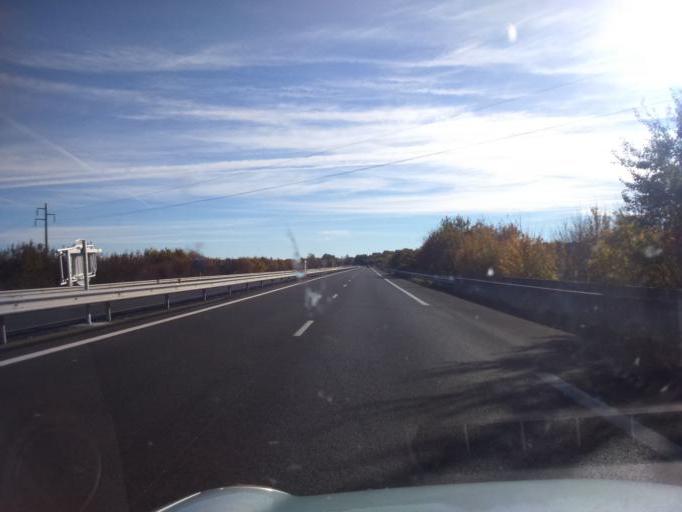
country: FR
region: Poitou-Charentes
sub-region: Departement de la Charente-Maritime
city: Tonnay-Charente
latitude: 45.9562
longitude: -0.9099
